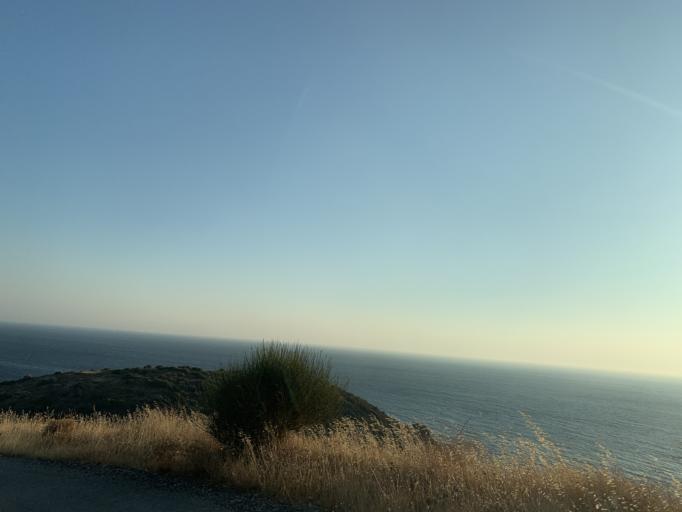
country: GR
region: North Aegean
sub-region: Chios
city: Psara
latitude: 38.5233
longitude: 25.8491
